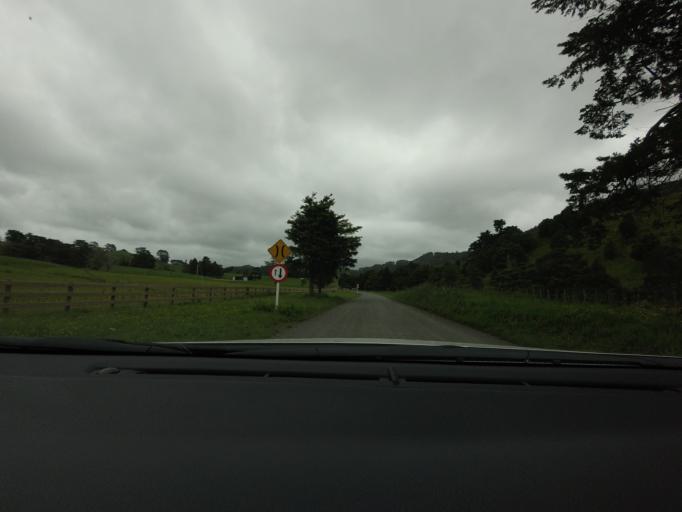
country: NZ
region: Auckland
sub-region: Auckland
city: Warkworth
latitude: -36.4800
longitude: 174.5863
